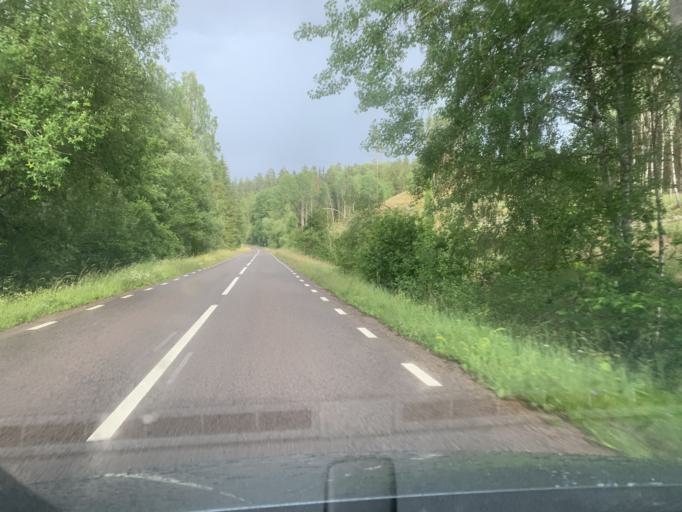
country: SE
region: Kalmar
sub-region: Vasterviks Kommun
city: Overum
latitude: 58.0208
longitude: 16.1340
